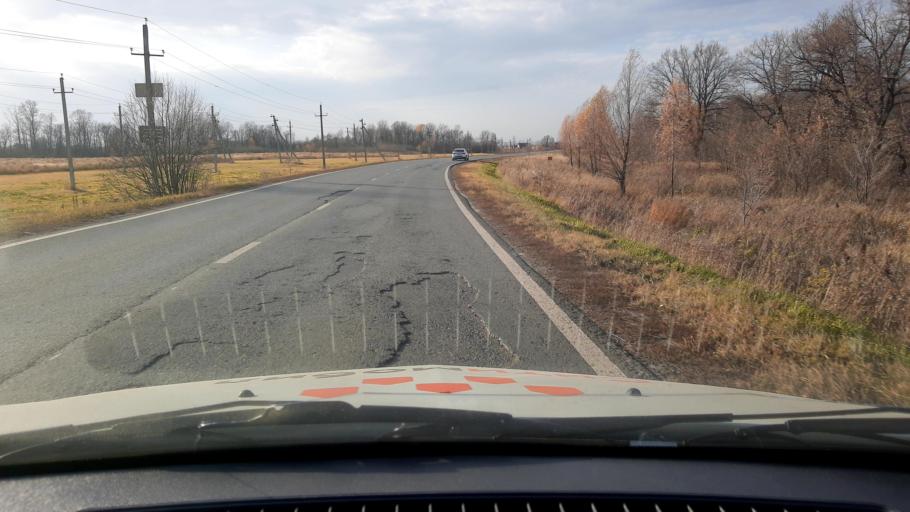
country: RU
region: Bashkortostan
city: Iglino
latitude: 54.7415
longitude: 56.2264
